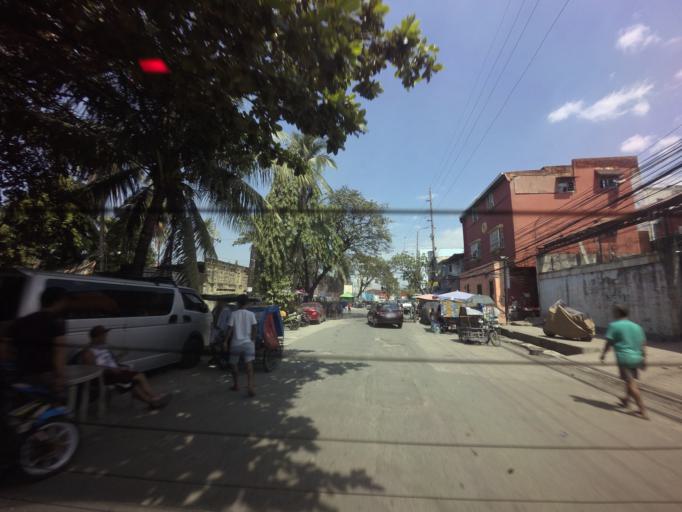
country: PH
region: Metro Manila
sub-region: Caloocan City
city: Niugan
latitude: 14.6340
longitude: 120.9657
